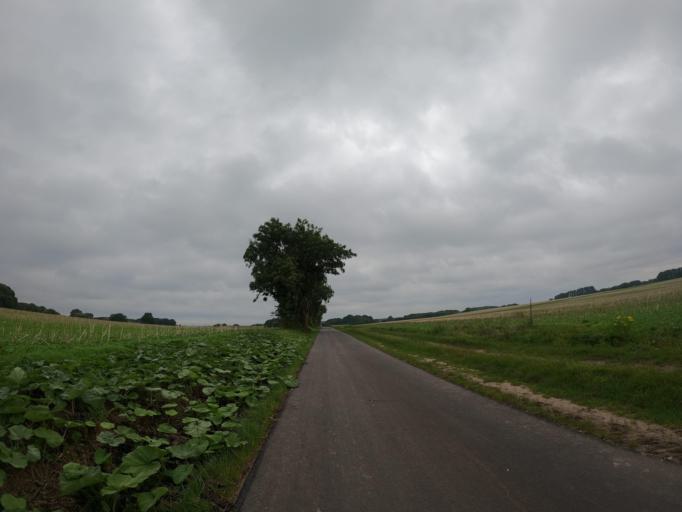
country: DE
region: Mecklenburg-Vorpommern
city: Poseritz
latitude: 54.2906
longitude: 13.2232
